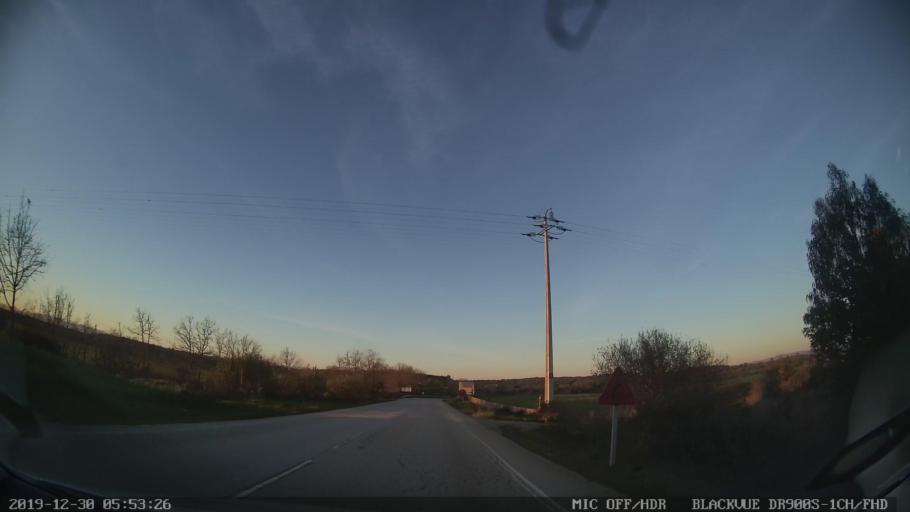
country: PT
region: Castelo Branco
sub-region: Idanha-A-Nova
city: Idanha-a-Nova
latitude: 40.0156
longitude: -7.2514
